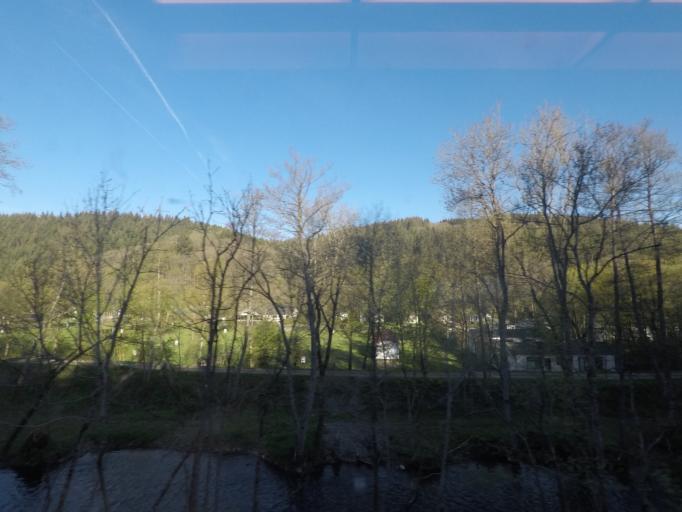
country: BE
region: Wallonia
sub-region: Province du Luxembourg
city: Nassogne
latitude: 50.0994
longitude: 5.2911
